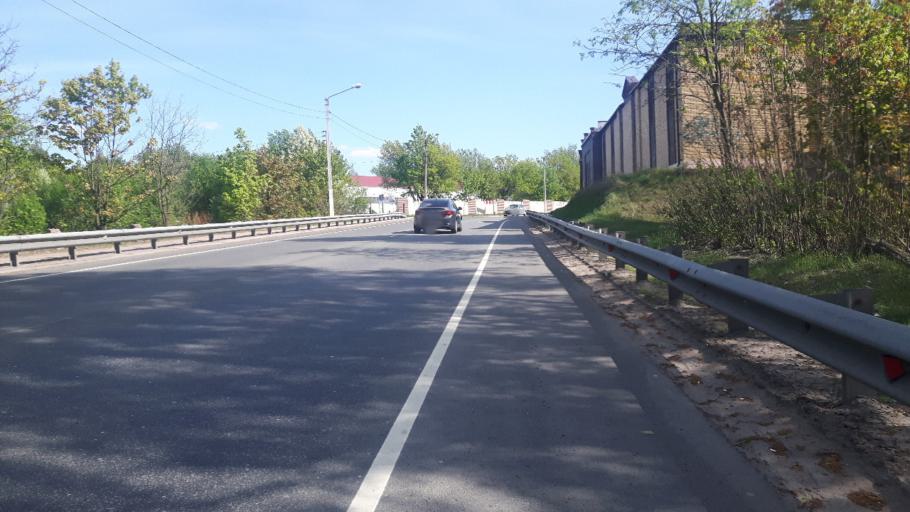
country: RU
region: Leningrad
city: Vyborg
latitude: 60.7225
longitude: 28.7156
